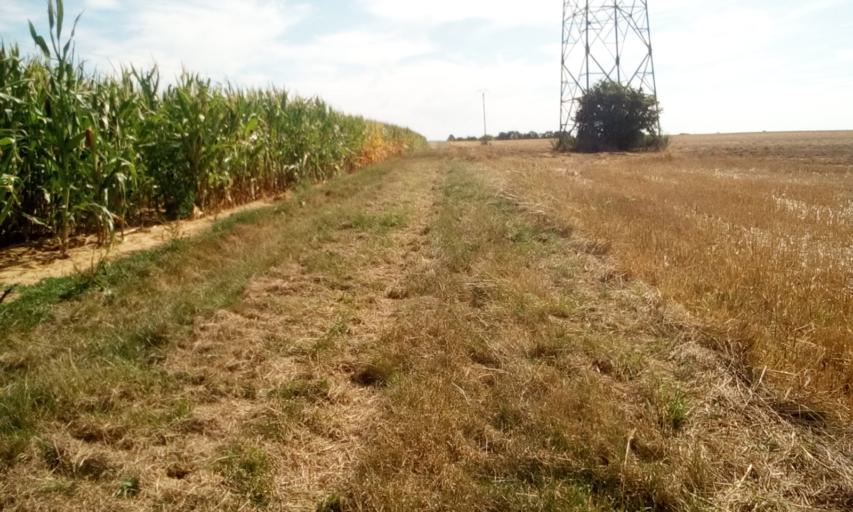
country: FR
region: Lower Normandy
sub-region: Departement du Calvados
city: Eterville
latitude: 49.1199
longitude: -0.4316
